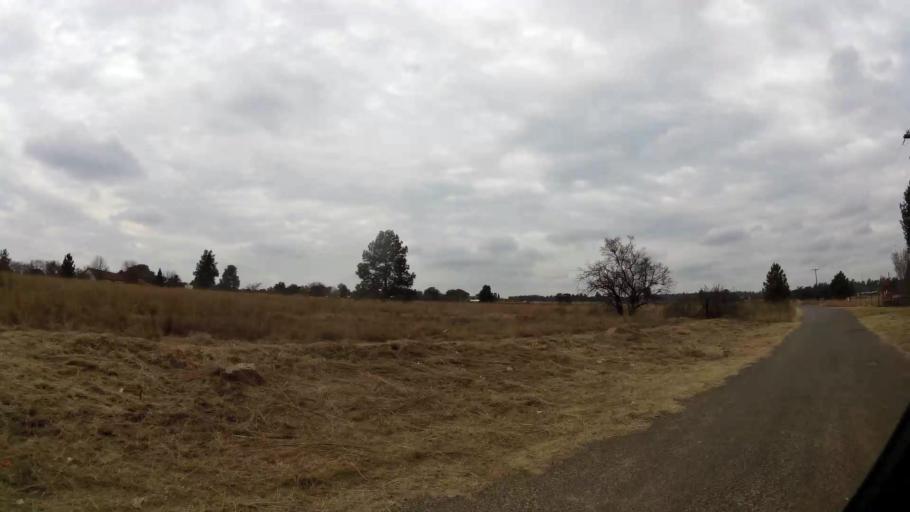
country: ZA
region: Gauteng
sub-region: West Rand District Municipality
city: Muldersdriseloop
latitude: -26.0541
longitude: 27.8774
